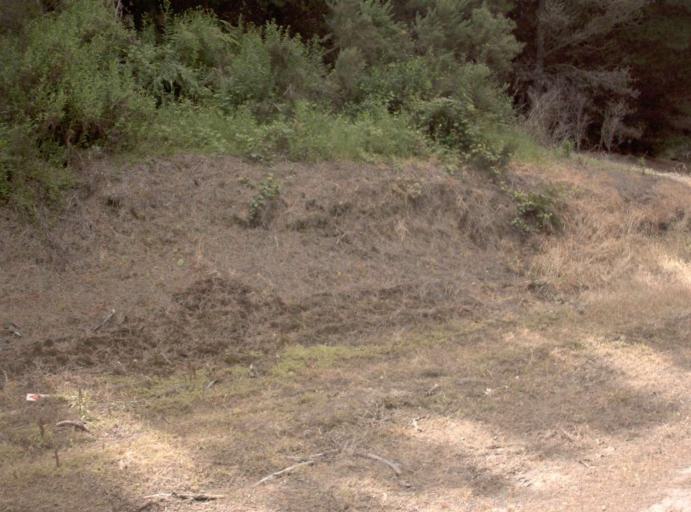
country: AU
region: Victoria
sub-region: Latrobe
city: Traralgon
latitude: -38.3866
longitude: 146.6629
